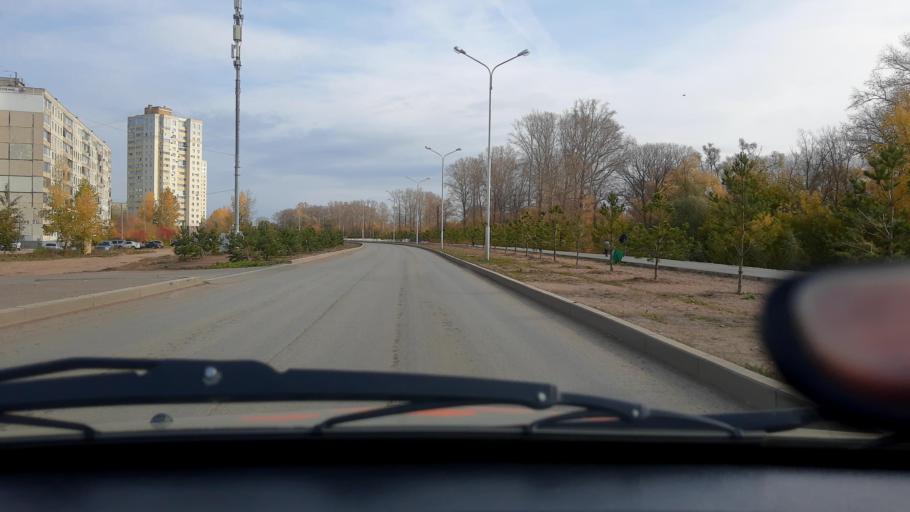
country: RU
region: Bashkortostan
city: Ufa
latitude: 54.7617
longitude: 56.0715
